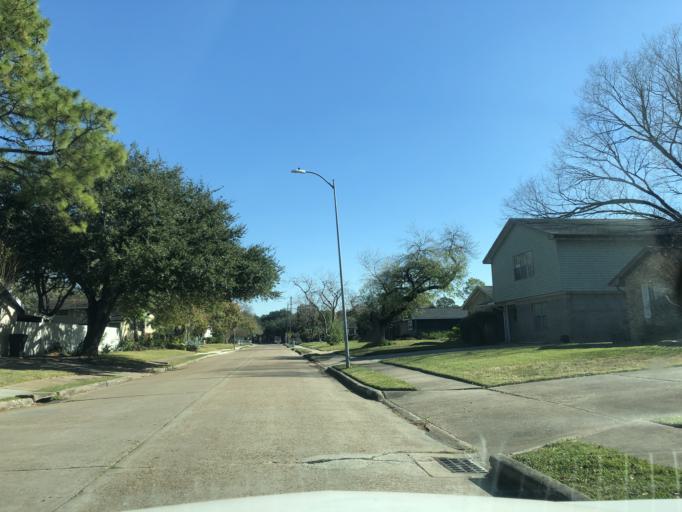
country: US
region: Texas
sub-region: Harris County
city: Bellaire
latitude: 29.6987
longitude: -95.5058
